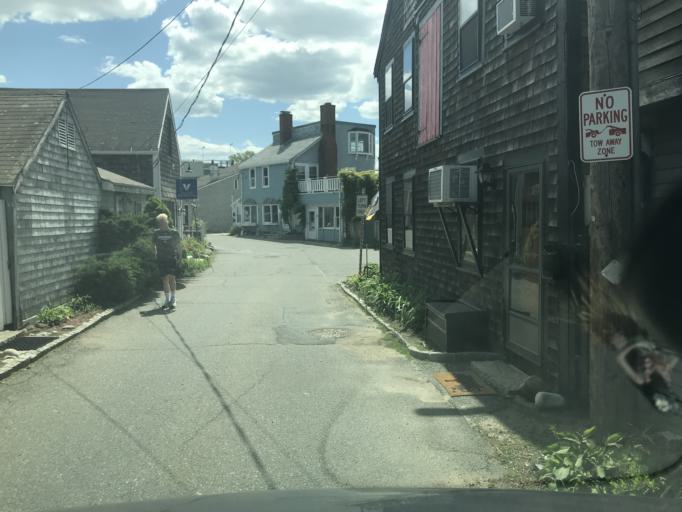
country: US
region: Massachusetts
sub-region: Essex County
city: Rockport
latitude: 42.6598
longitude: -70.6161
